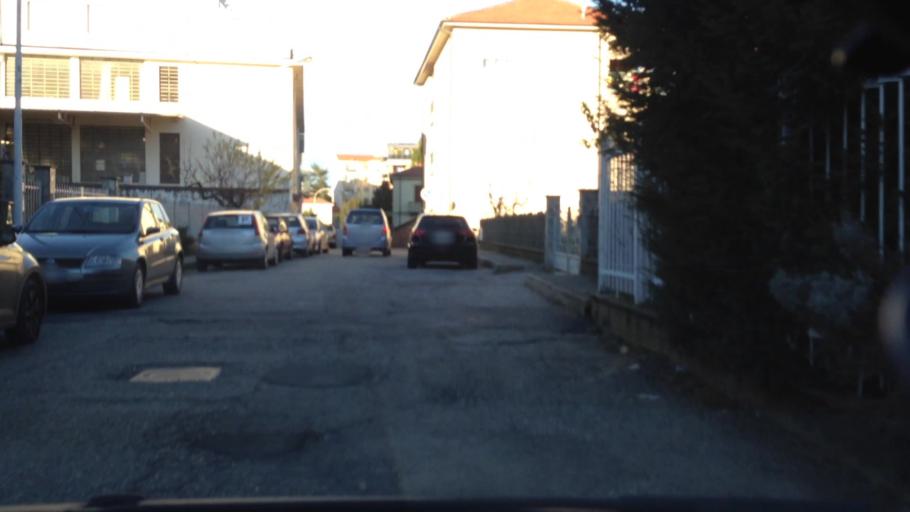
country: IT
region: Piedmont
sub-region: Provincia di Torino
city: Chieri
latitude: 45.0063
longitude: 7.8183
